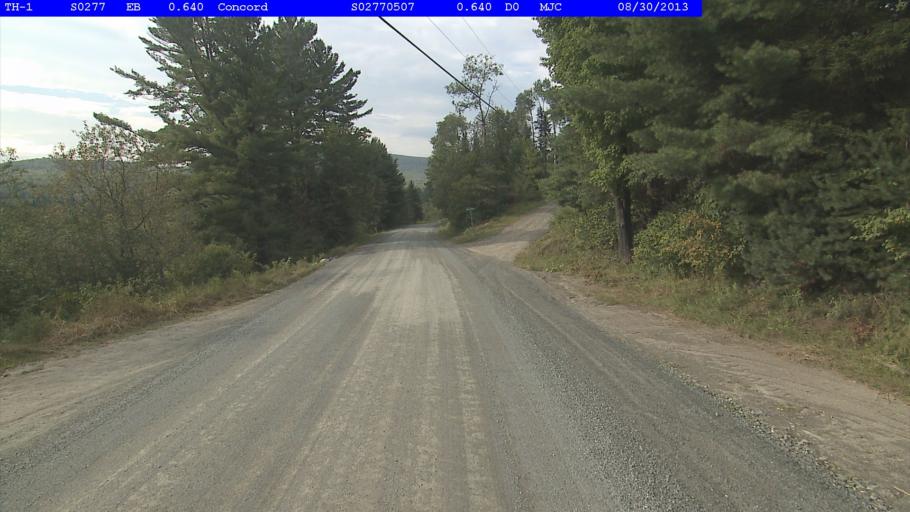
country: US
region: Vermont
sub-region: Caledonia County
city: Lyndonville
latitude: 44.4726
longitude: -71.8618
